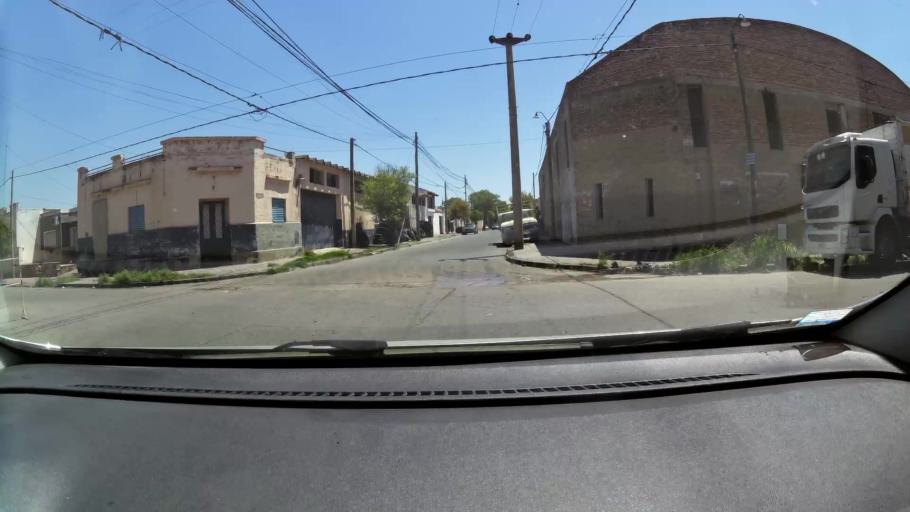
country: AR
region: Cordoba
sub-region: Departamento de Capital
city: Cordoba
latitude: -31.3905
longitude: -64.1453
